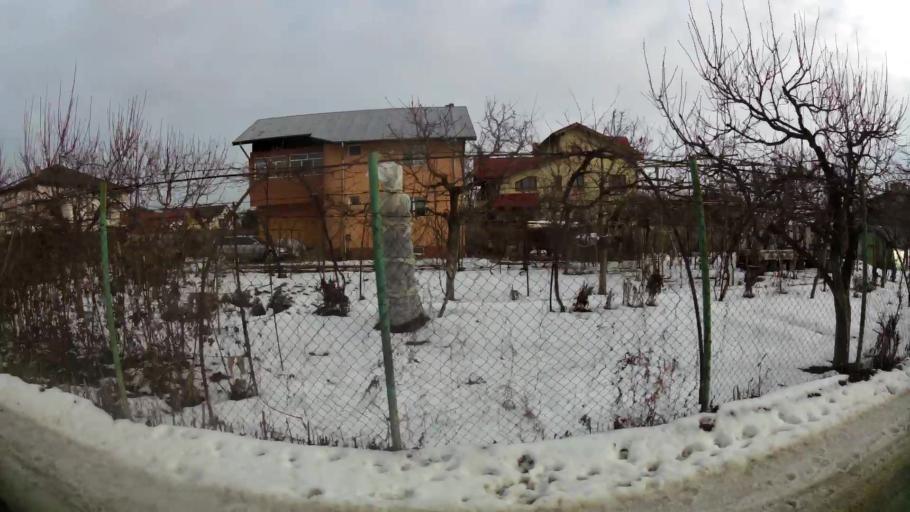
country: RO
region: Ilfov
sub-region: Comuna Popesti-Leordeni
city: Popesti-Leordeni
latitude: 44.4022
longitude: 26.1763
